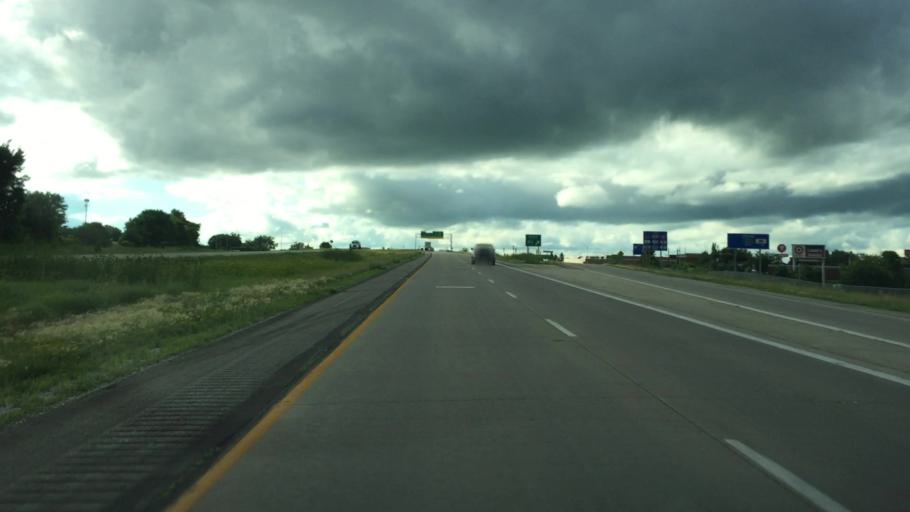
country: US
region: Iowa
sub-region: Polk County
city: Altoona
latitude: 41.6403
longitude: -93.5076
